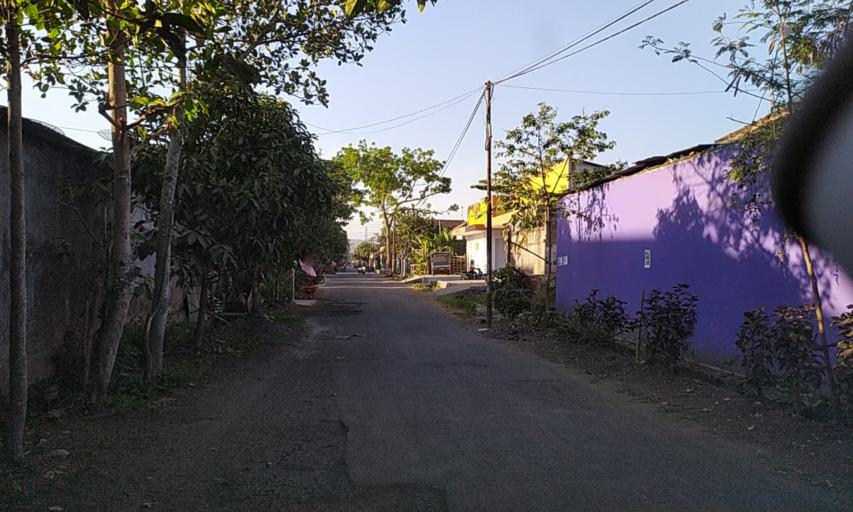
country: ID
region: Central Java
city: Sidareja
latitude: -7.4850
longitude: 108.7931
